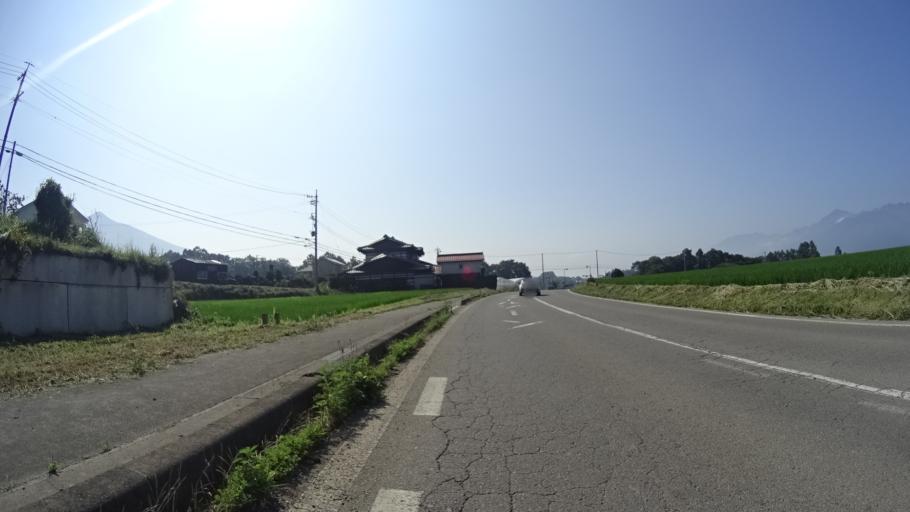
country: JP
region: Nagano
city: Chino
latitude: 35.9356
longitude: 138.2609
